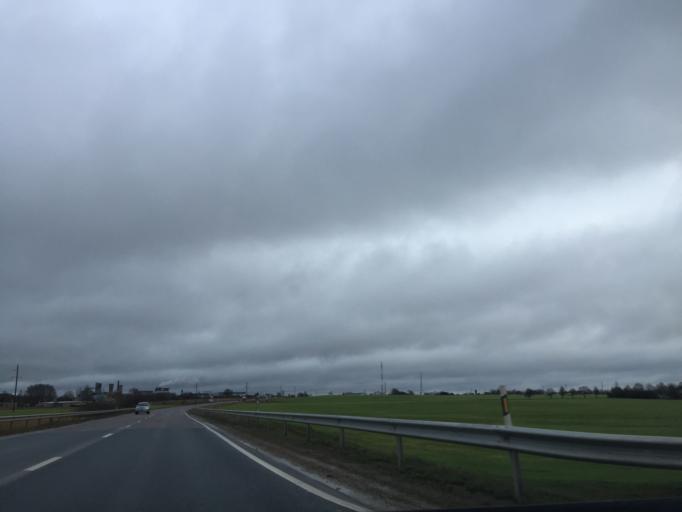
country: LV
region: Saldus Rajons
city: Saldus
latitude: 56.6776
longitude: 22.4482
